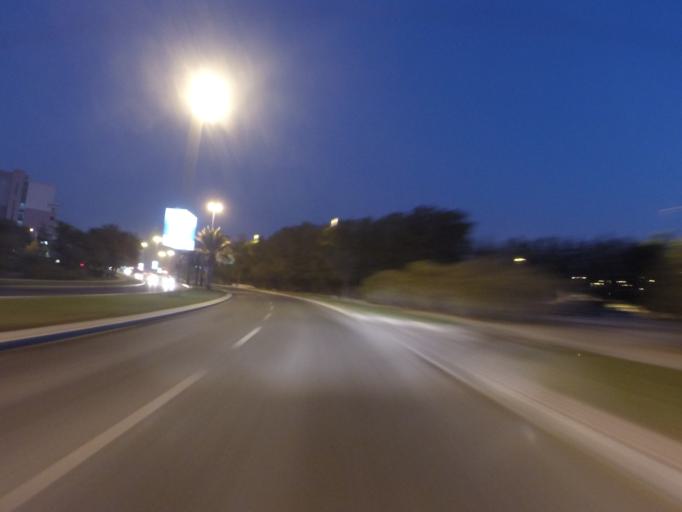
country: AE
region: Dubai
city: Dubai
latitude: 25.0497
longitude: 55.1269
